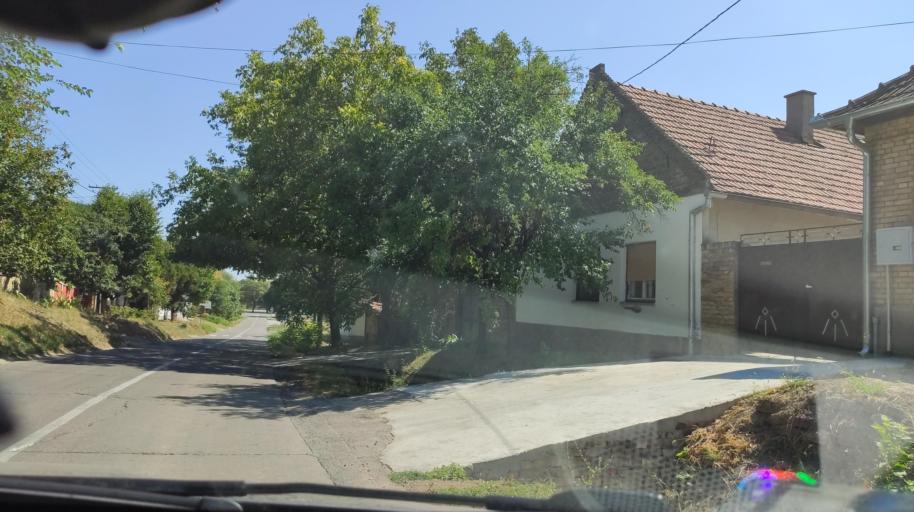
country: RS
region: Autonomna Pokrajina Vojvodina
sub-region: Severnobacki Okrug
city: Backa Topola
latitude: 45.8067
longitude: 19.6280
